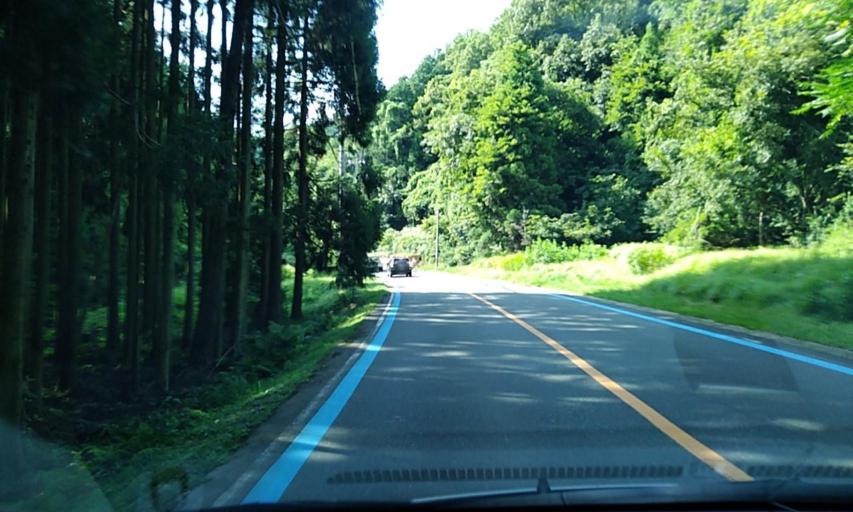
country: JP
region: Kyoto
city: Ayabe
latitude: 35.3063
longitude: 135.2940
